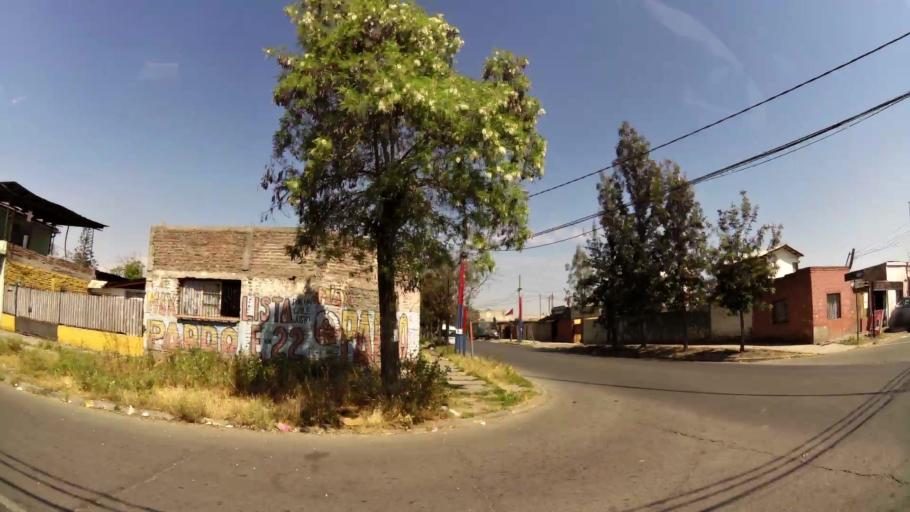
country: CL
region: Santiago Metropolitan
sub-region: Provincia de Santiago
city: La Pintana
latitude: -33.5333
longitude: -70.6493
